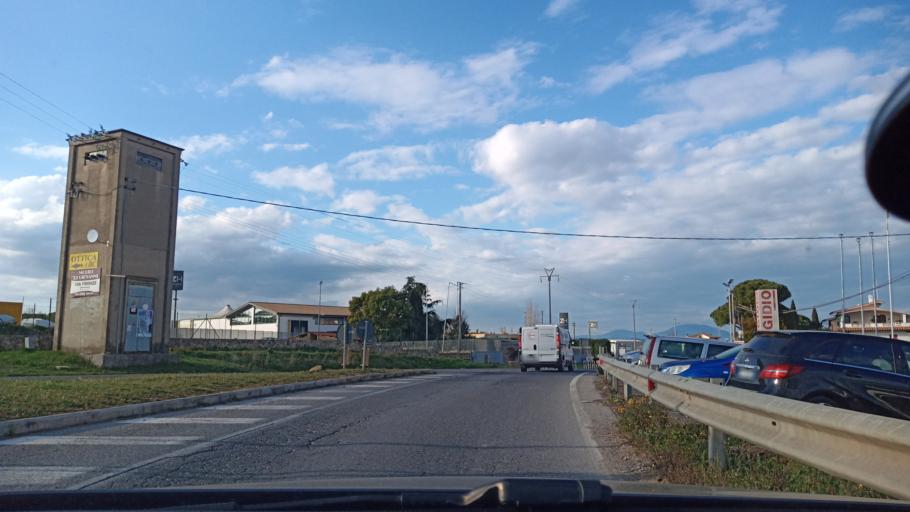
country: IT
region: Latium
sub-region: Citta metropolitana di Roma Capitale
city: Fiano Romano
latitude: 42.1516
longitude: 12.6157
